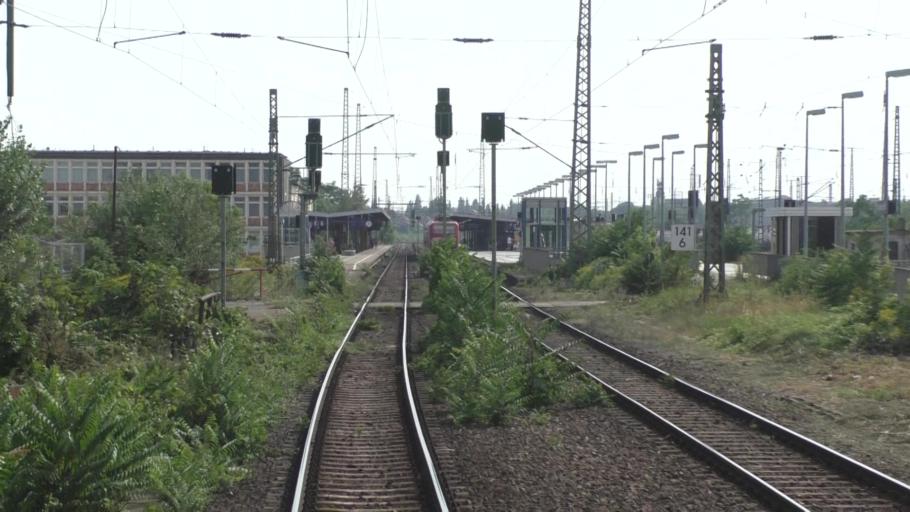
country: DE
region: Saxony-Anhalt
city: Magdeburg
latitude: 52.1330
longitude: 11.6272
